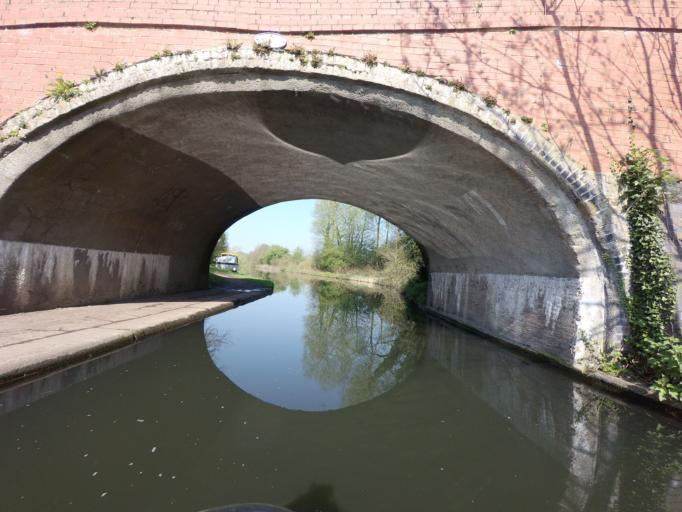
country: GB
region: England
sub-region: Hertfordshire
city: Bovingdon
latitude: 51.7502
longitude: -0.5291
